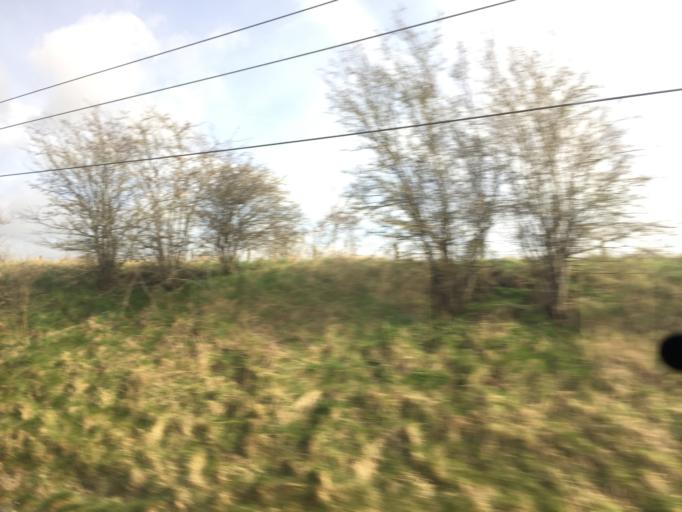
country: GB
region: England
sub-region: Cumbria
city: Penrith
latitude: 54.7346
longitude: -2.8027
